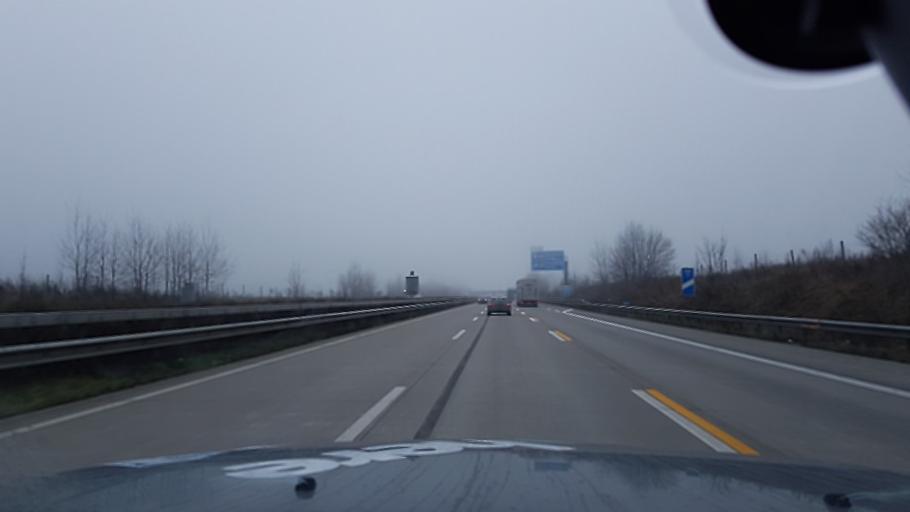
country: DE
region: Lower Saxony
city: Buehren
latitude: 52.8199
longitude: 8.2123
